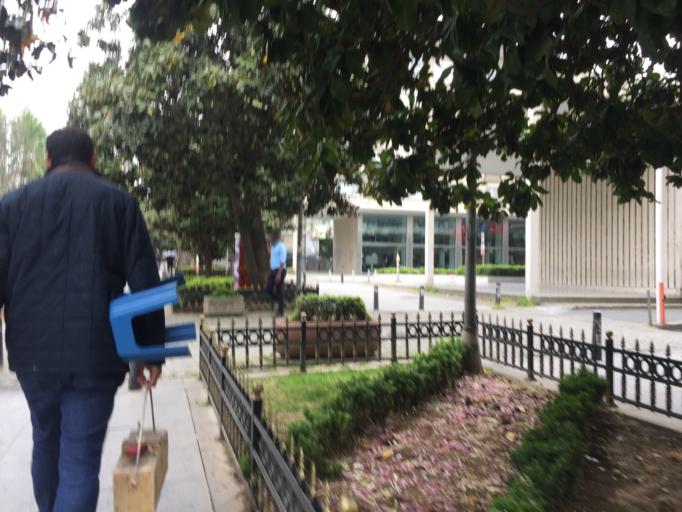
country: TR
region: Istanbul
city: Sisli
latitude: 41.0432
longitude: 28.9866
